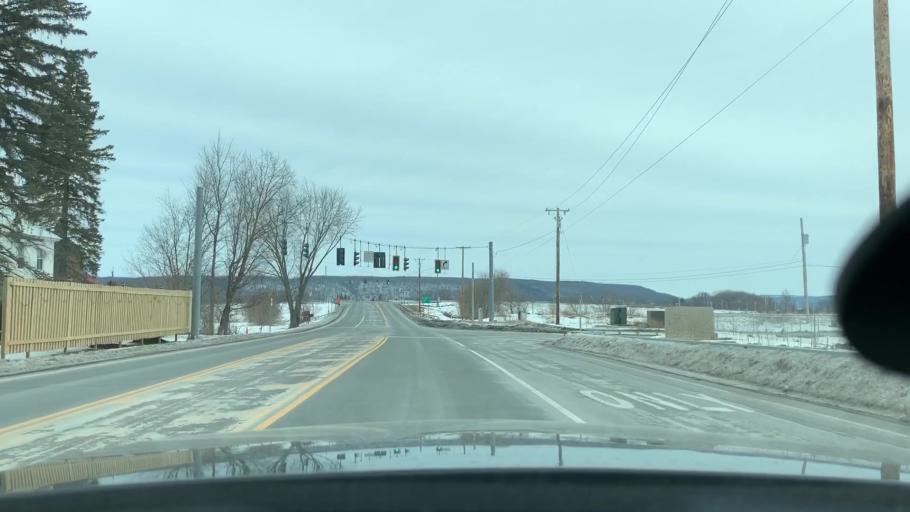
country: US
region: New York
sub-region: Herkimer County
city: Frankfort
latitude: 43.0394
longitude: -75.0890
